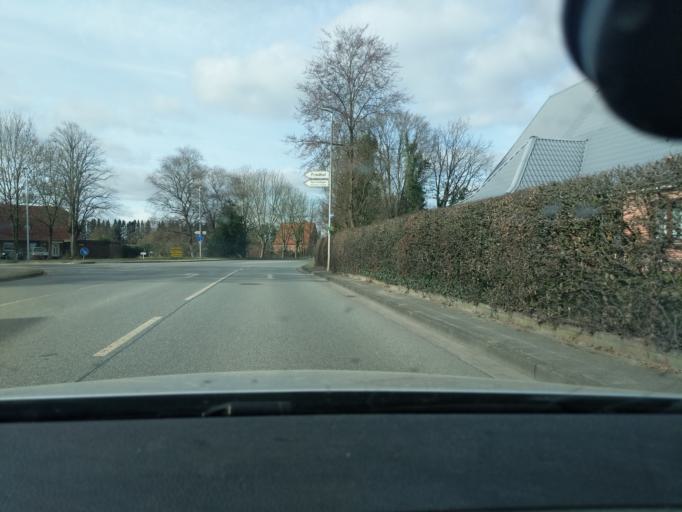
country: DE
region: Lower Saxony
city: Stade
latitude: 53.6558
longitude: 9.4776
